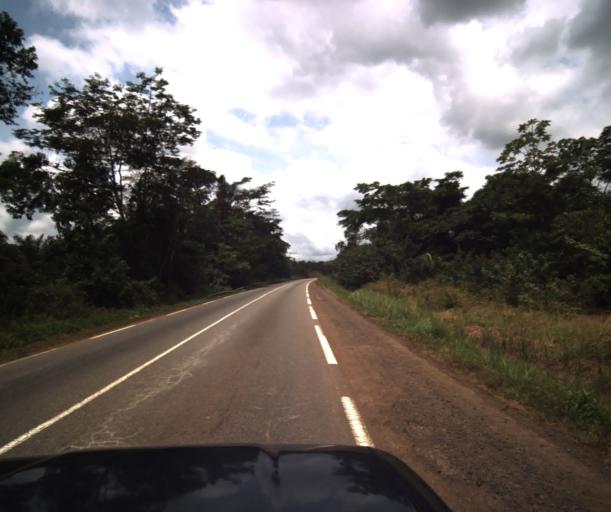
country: CM
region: Centre
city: Eseka
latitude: 3.8466
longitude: 10.9731
